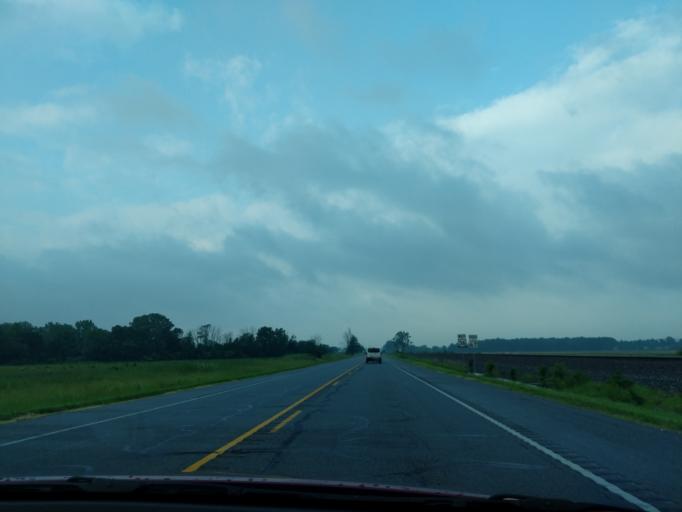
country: US
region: Indiana
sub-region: Hancock County
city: McCordsville
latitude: 39.9088
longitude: -85.8961
